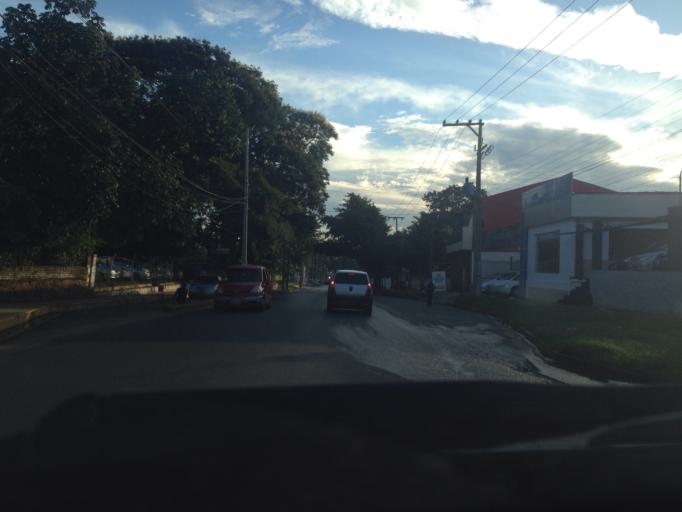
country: PY
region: Central
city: Lambare
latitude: -25.3309
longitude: -57.5869
